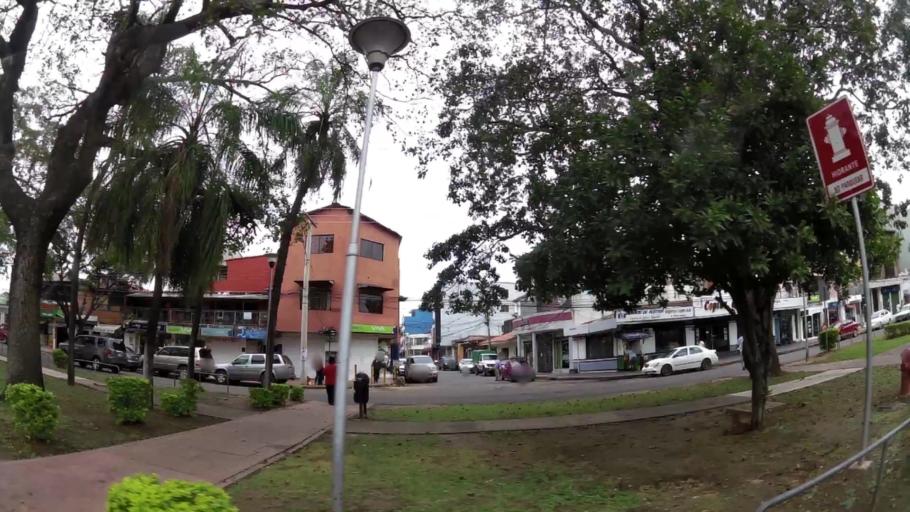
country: BO
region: Santa Cruz
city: Santa Cruz de la Sierra
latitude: -17.7745
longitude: -63.1788
